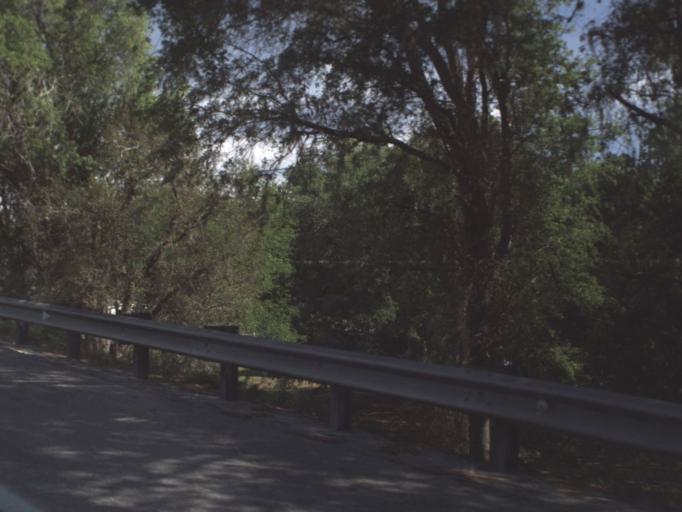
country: US
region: Florida
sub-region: Lake County
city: Lady Lake
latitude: 28.9263
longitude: -81.9246
